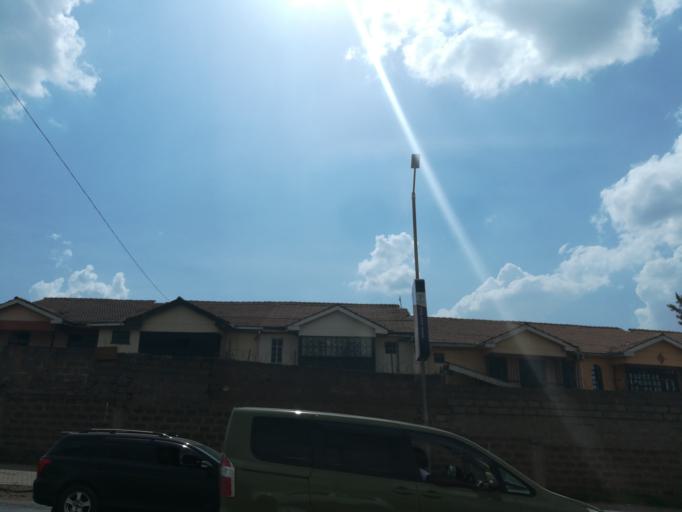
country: KE
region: Nairobi Area
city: Pumwani
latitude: -1.3183
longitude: 36.8536
